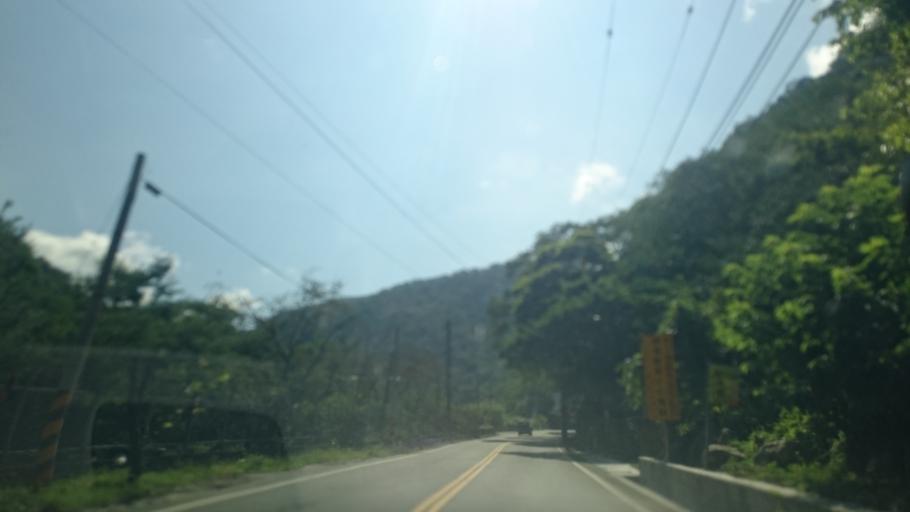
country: TW
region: Taiwan
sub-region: Nantou
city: Puli
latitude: 23.9980
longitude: 121.0464
